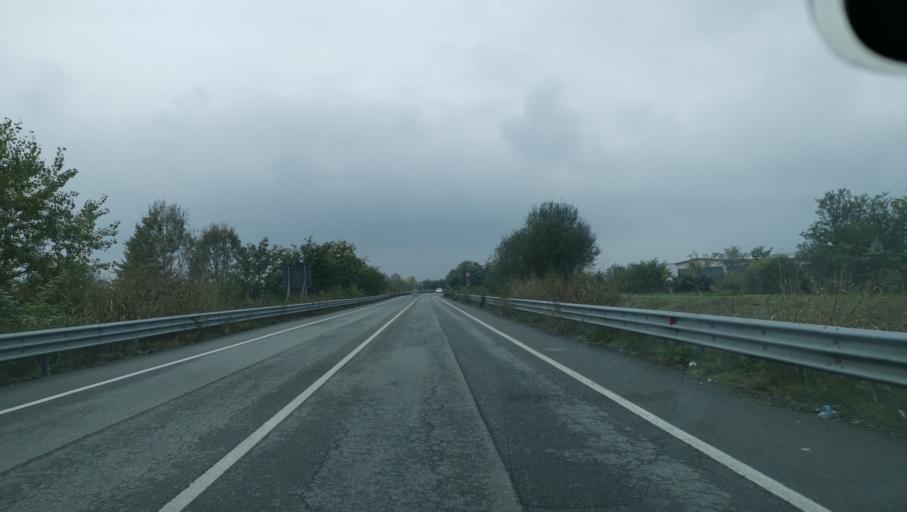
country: IT
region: Piedmont
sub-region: Provincia di Torino
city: San Raffaele Cimena
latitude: 45.1444
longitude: 7.8388
